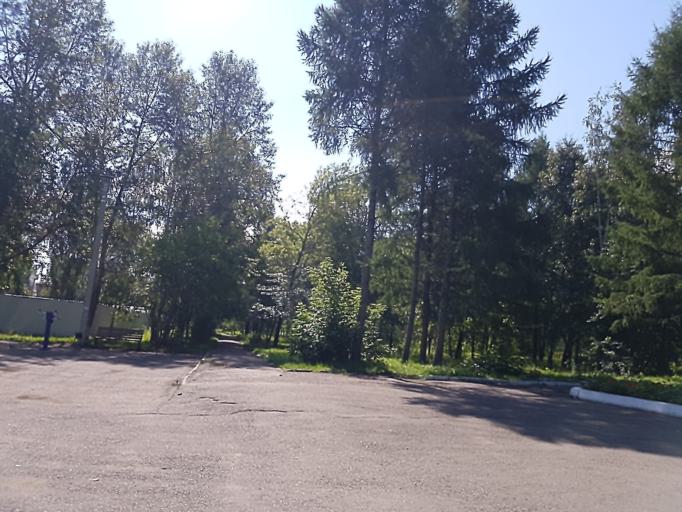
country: RU
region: Irkutsk
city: Usol'ye-Sibirskoye
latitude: 52.7565
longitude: 103.6350
